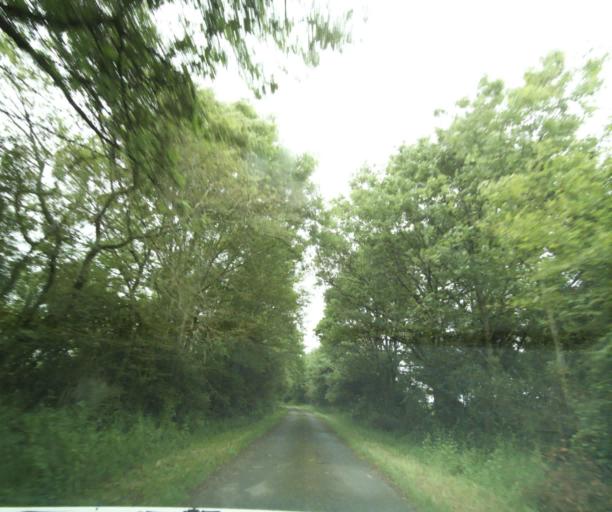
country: FR
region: Bourgogne
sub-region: Departement de Saone-et-Loire
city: Palinges
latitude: 46.5732
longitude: 4.2070
